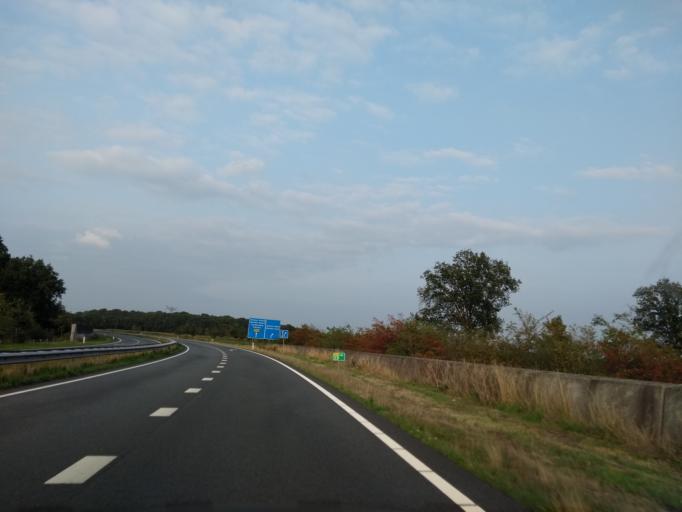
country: NL
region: Overijssel
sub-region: Gemeente Wierden
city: Wierden
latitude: 52.3441
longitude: 6.6036
